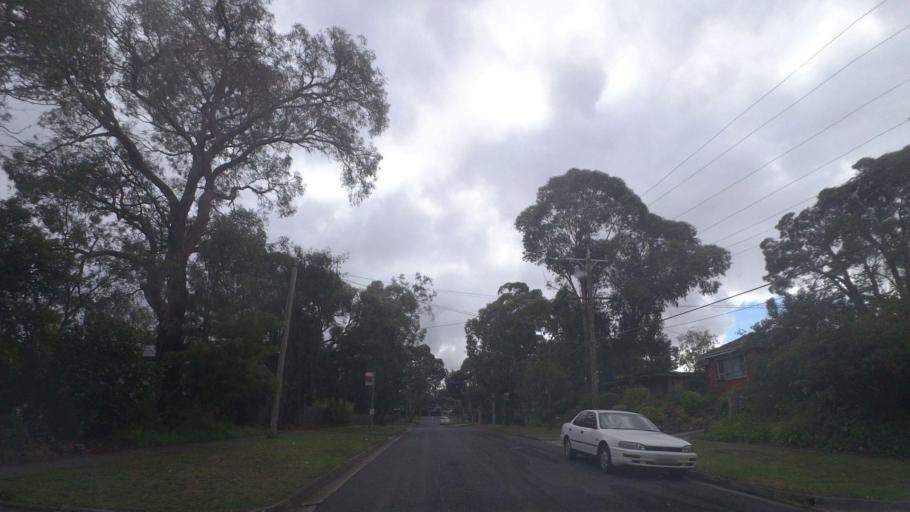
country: AU
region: Victoria
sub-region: Whitehorse
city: Forest Hill
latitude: -37.8319
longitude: 145.1657
